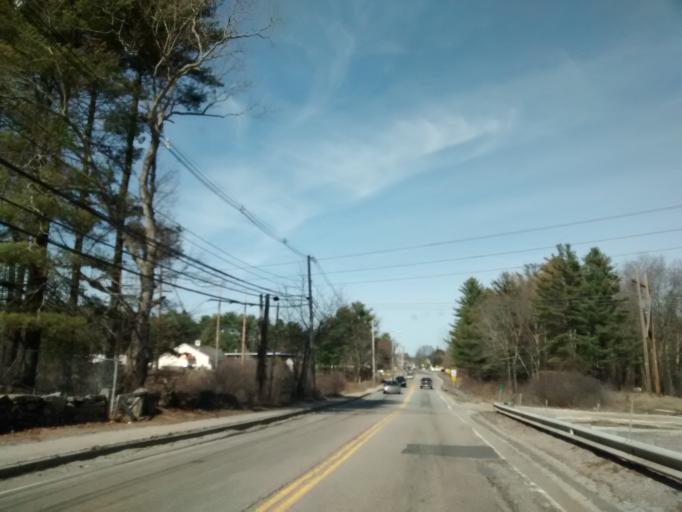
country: US
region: Massachusetts
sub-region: Norfolk County
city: Bellingham
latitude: 42.1173
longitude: -71.4587
